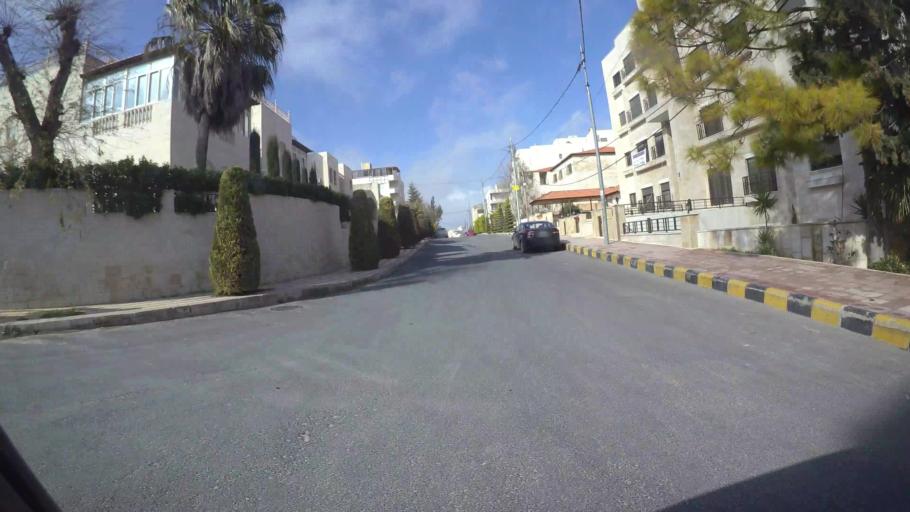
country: JO
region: Amman
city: Al Jubayhah
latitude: 32.0406
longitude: 35.8725
